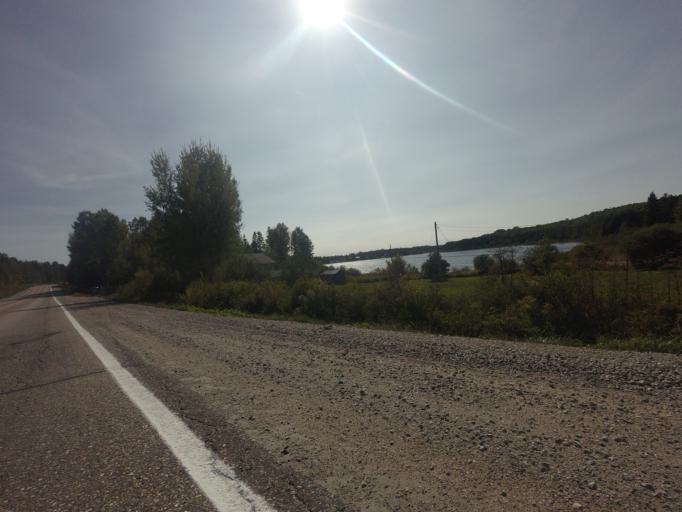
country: CA
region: Quebec
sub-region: Outaouais
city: Maniwaki
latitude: 46.4891
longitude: -75.8212
